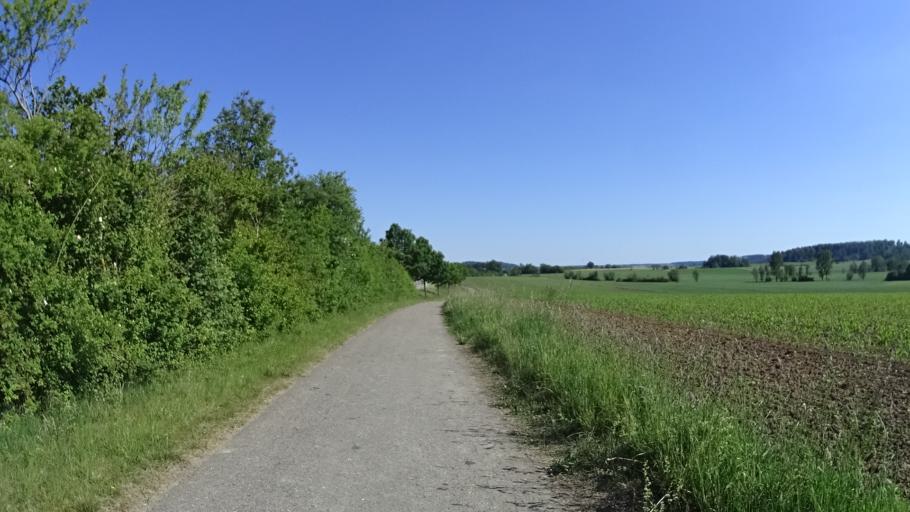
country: DE
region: Bavaria
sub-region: Regierungsbezirk Mittelfranken
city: Dombuhl
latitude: 49.2116
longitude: 10.3070
